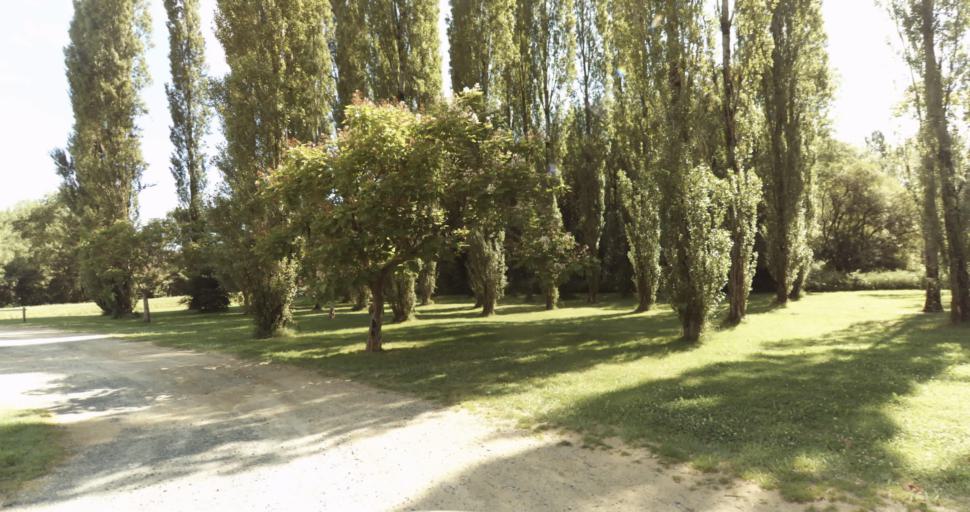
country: FR
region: Aquitaine
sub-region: Departement de la Gironde
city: Bazas
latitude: 44.4422
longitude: -0.1698
